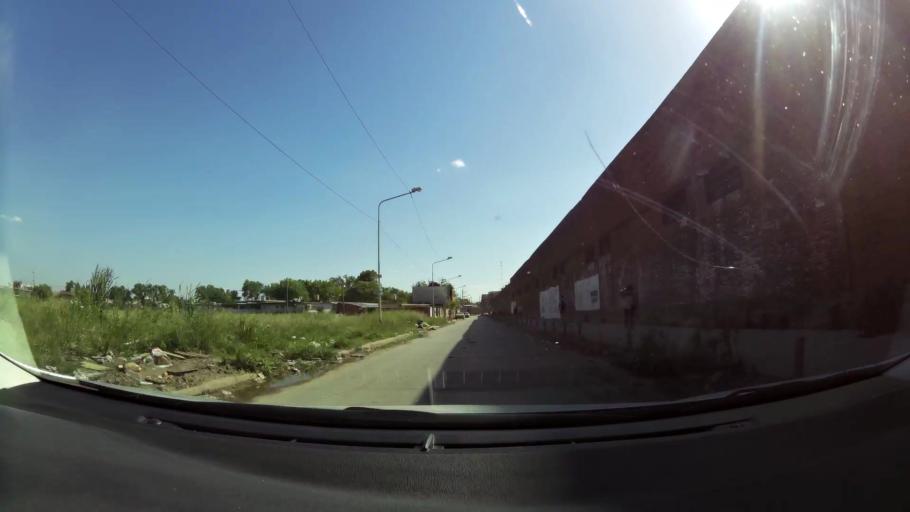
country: AR
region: Buenos Aires F.D.
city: Villa Lugano
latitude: -34.7059
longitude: -58.4801
